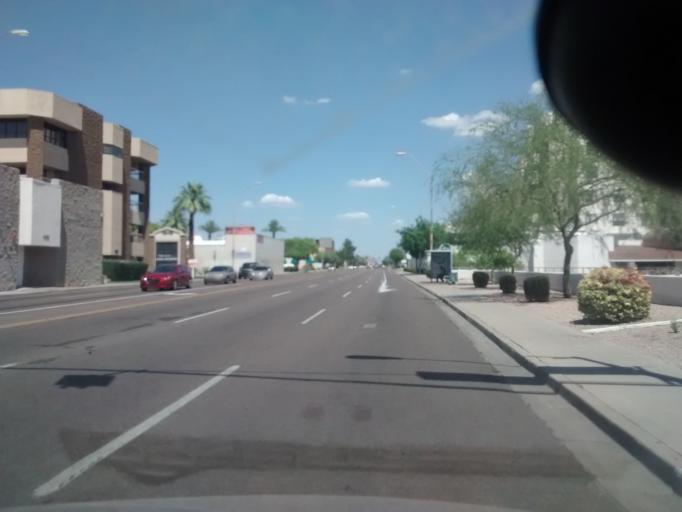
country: US
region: Arizona
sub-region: Maricopa County
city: Phoenix
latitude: 33.4657
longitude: -112.0607
